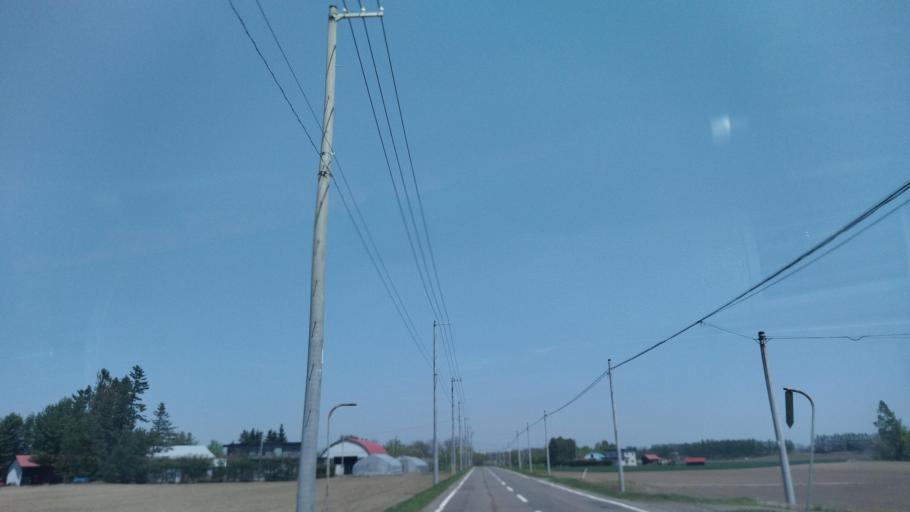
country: JP
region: Hokkaido
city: Obihiro
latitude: 42.8908
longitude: 143.0273
